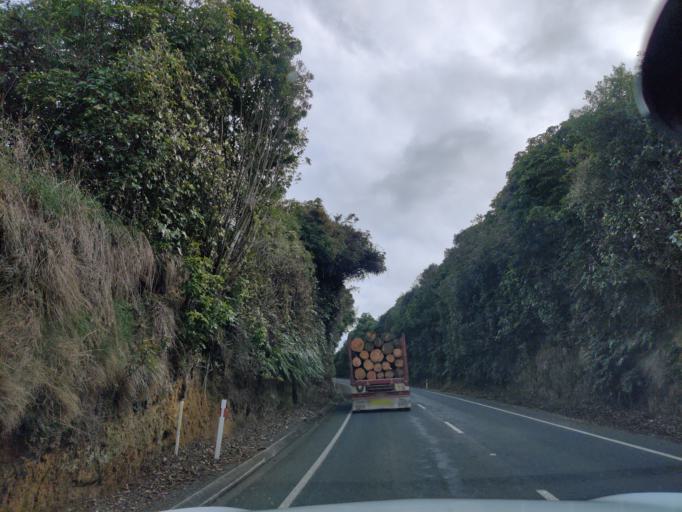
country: NZ
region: Waikato
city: Turangi
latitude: -38.8053
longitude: 175.6913
